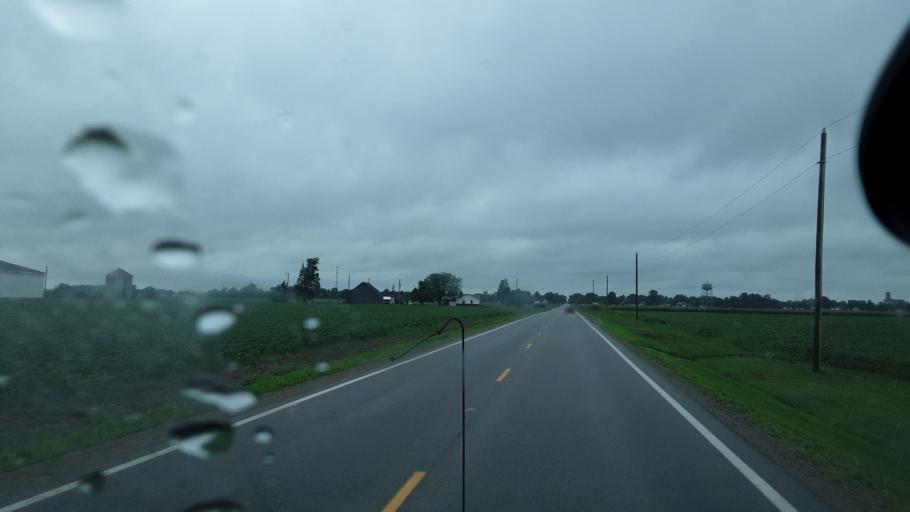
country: US
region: Ohio
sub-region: Mercer County
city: Rockford
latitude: 40.7574
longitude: -84.6262
